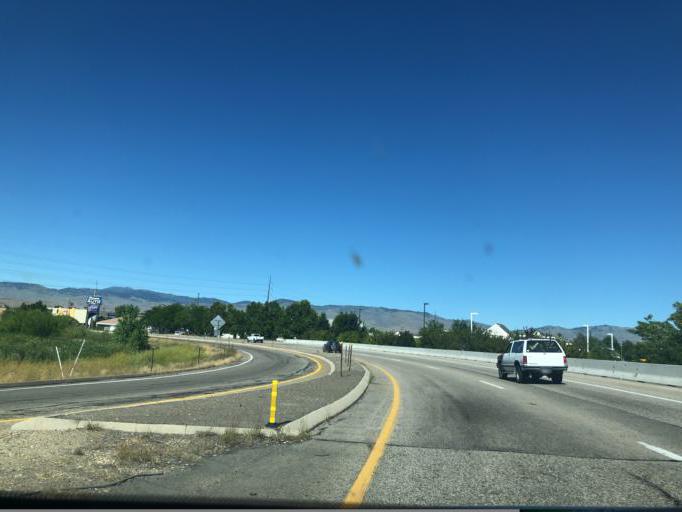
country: US
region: Idaho
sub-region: Ada County
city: Garden City
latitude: 43.6027
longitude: -116.2789
